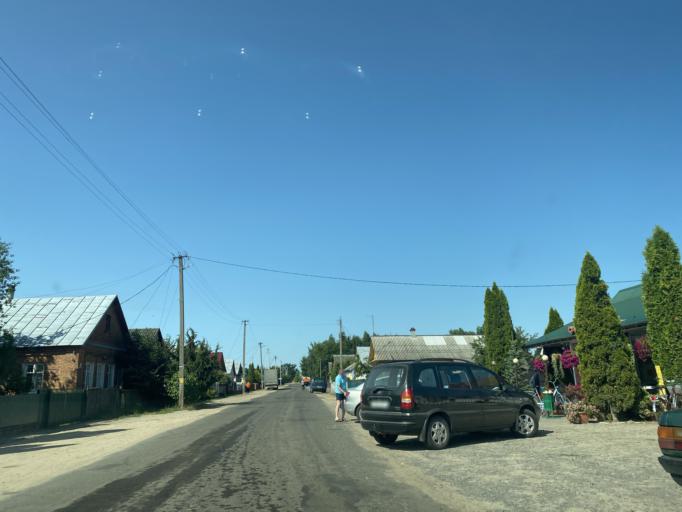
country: BY
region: Brest
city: Ivanava
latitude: 52.3166
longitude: 25.6048
